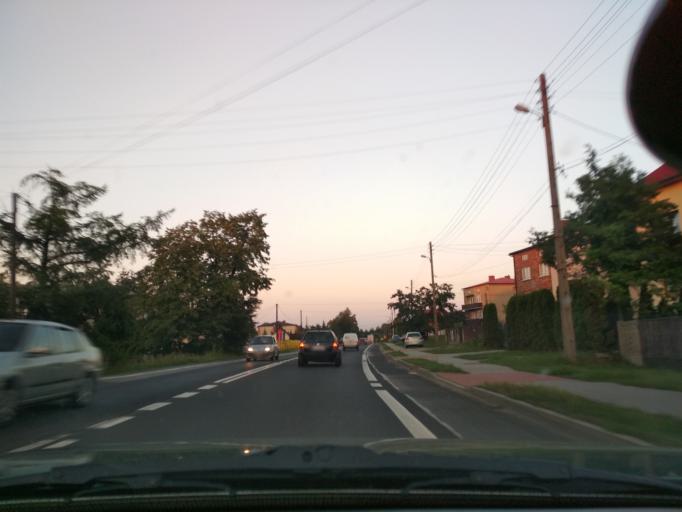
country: PL
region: Silesian Voivodeship
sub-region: Powiat zawiercianski
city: Poreba
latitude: 50.4889
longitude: 19.3033
